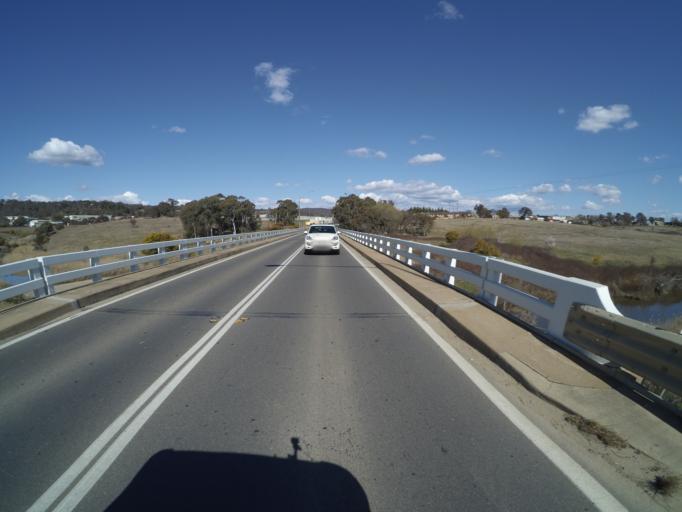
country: AU
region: New South Wales
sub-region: Queanbeyan
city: Queanbeyan
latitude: -35.3349
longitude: 149.2397
